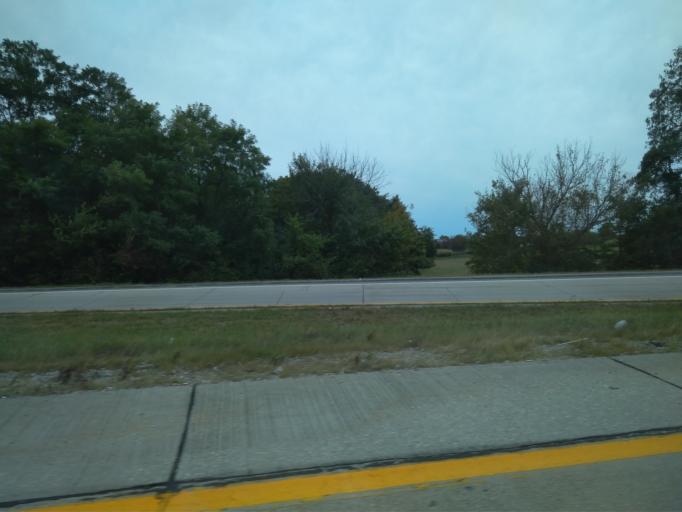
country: US
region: Kentucky
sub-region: Jefferson County
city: Anchorage
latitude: 38.2844
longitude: -85.5121
